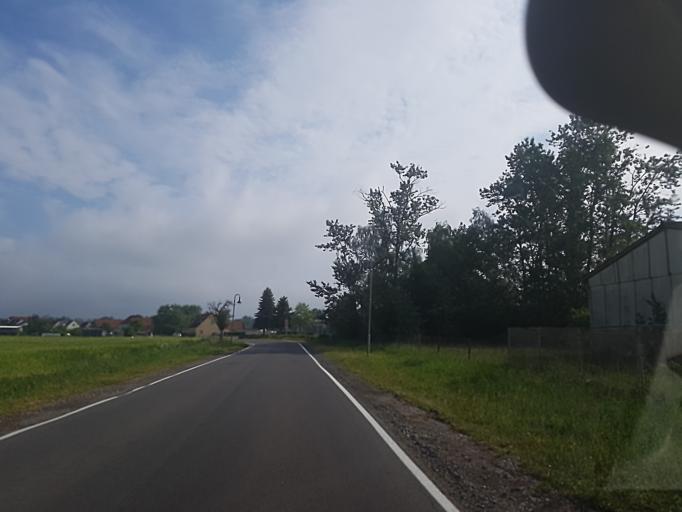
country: DE
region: Saxony-Anhalt
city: Lindau
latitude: 52.0219
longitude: 12.2246
